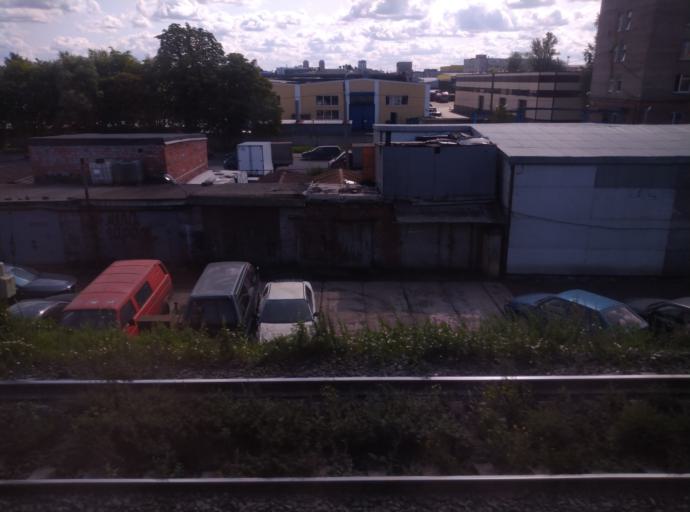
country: RU
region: St.-Petersburg
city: Centralniy
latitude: 59.9086
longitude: 30.3866
